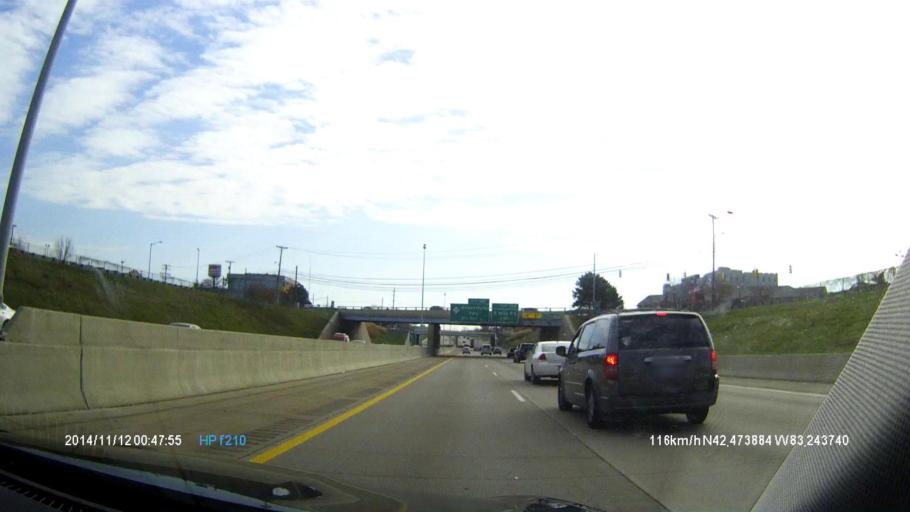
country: US
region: Michigan
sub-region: Oakland County
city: Southfield
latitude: 42.4738
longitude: -83.2436
